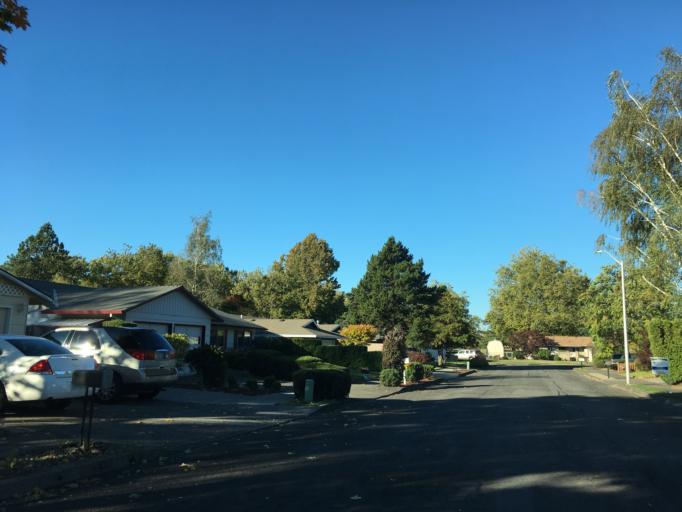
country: US
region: Oregon
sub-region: Multnomah County
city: Wood Village
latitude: 45.5121
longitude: -122.4042
